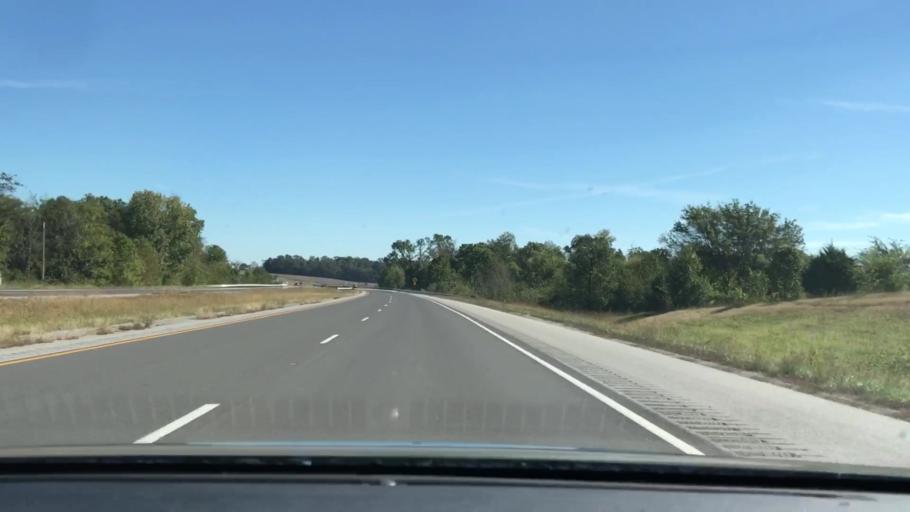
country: US
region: Kentucky
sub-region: Logan County
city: Russellville
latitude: 36.8147
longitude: -87.0126
